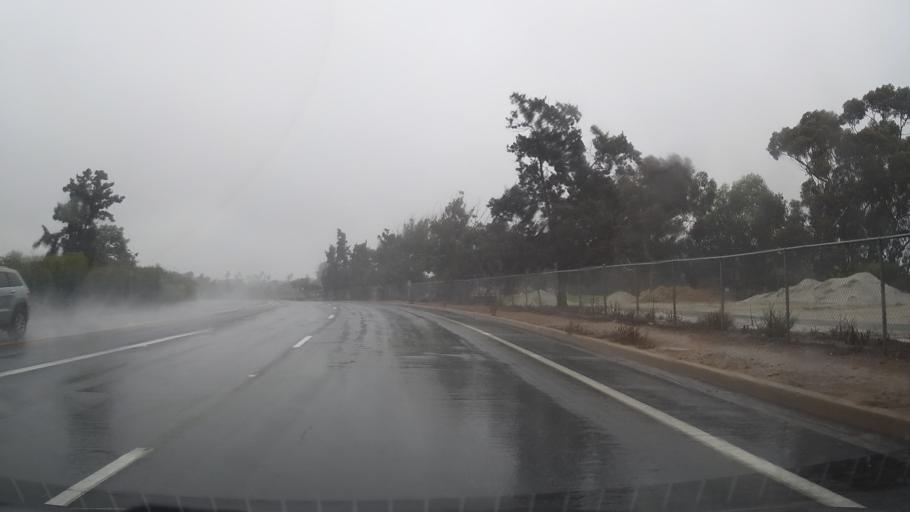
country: US
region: California
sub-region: San Diego County
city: San Diego
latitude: 32.7312
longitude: -117.1380
